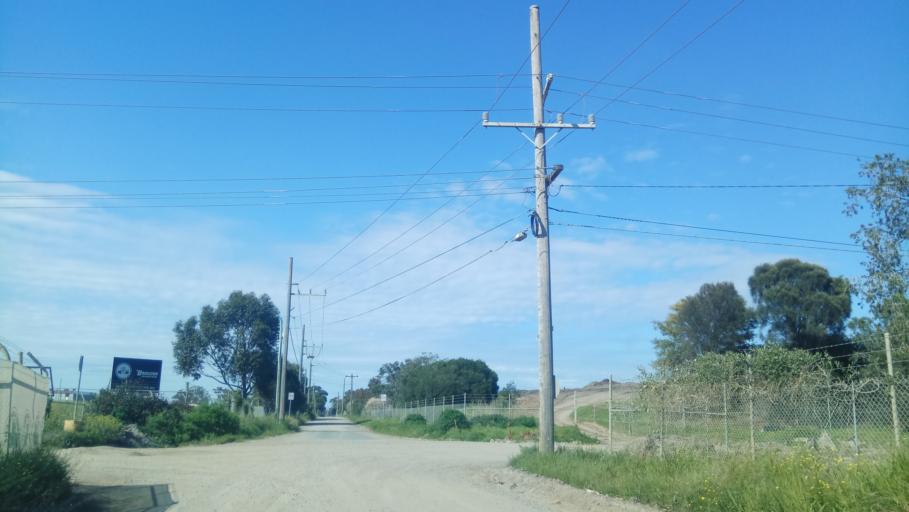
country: AU
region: Victoria
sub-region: Kingston
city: Clayton South
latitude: -37.9506
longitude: 145.1196
